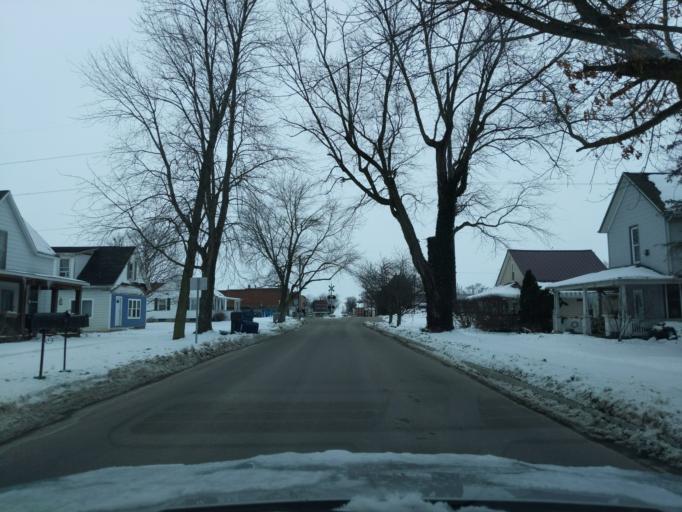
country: US
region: Indiana
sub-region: Benton County
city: Otterbein
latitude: 40.4877
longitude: -87.0962
